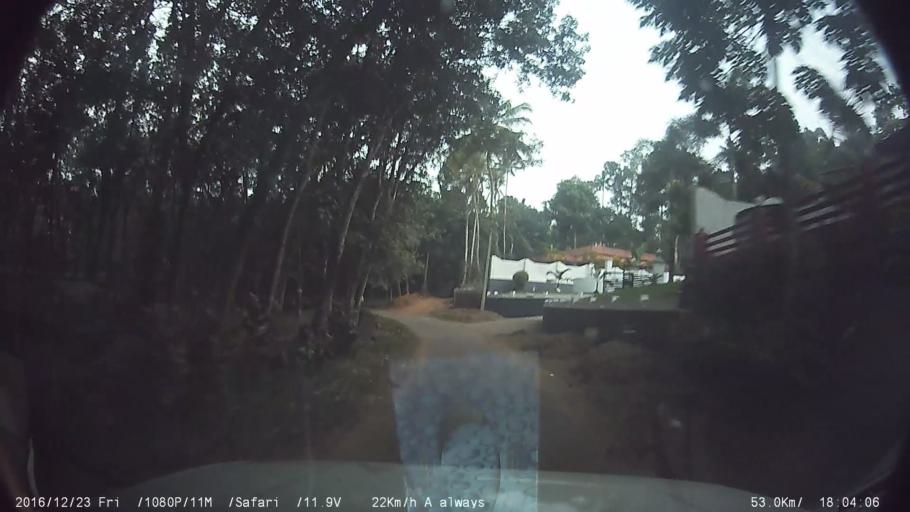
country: IN
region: Kerala
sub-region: Kottayam
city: Palackattumala
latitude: 9.7776
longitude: 76.5896
